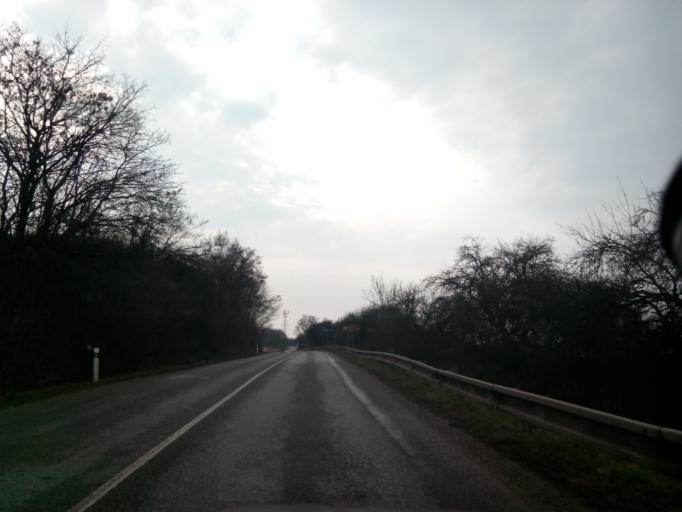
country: SK
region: Kosicky
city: Kosice
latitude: 48.6450
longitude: 21.3664
